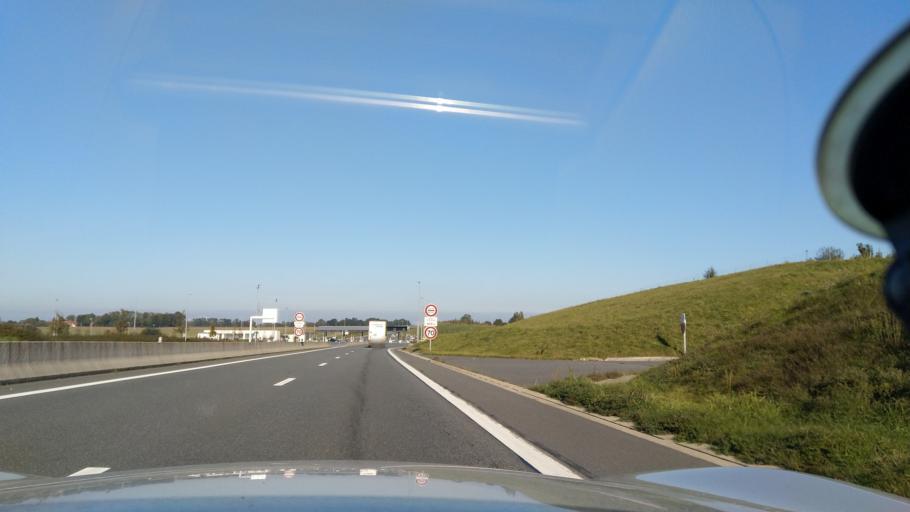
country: FR
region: Haute-Normandie
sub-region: Departement de la Seine-Maritime
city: Villers-Ecalles
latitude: 49.5453
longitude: 0.9252
